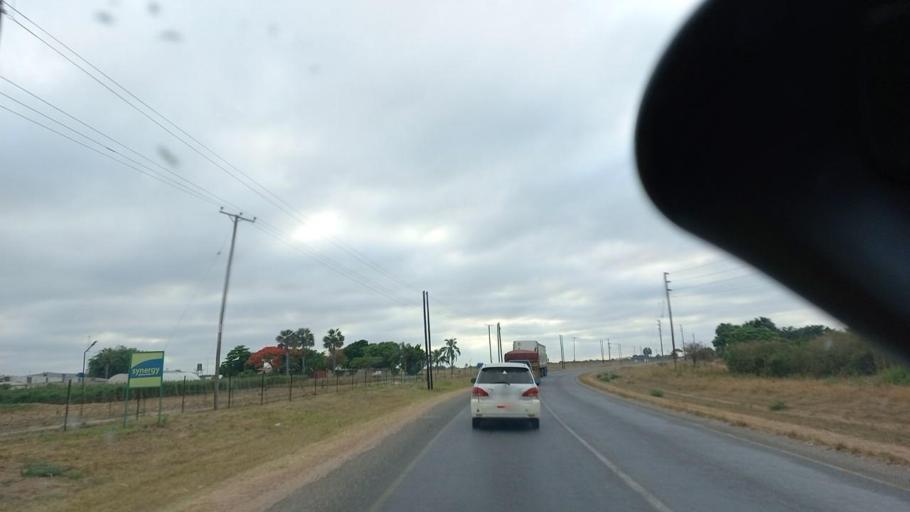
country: ZM
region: Lusaka
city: Chongwe
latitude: -15.3423
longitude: 28.5204
